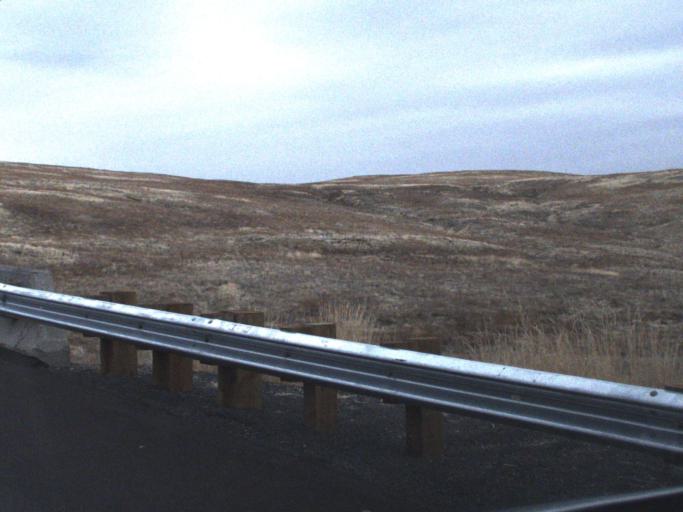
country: US
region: Washington
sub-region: Adams County
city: Ritzville
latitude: 46.7533
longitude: -118.2850
